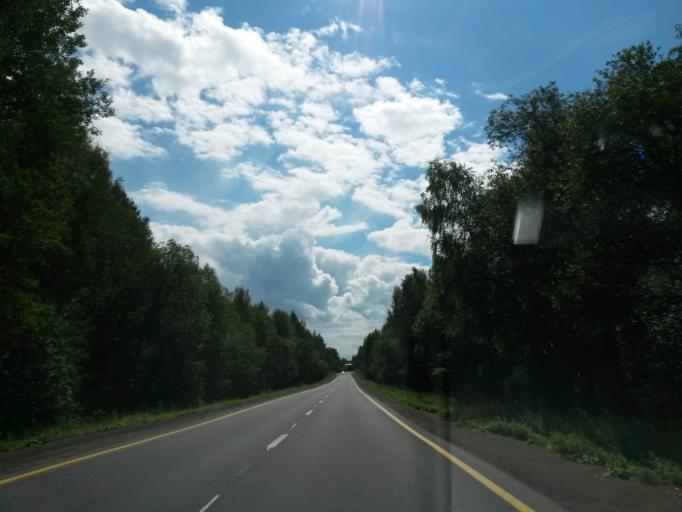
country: RU
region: Jaroslavl
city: Gavrilov-Yam
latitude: 57.2872
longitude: 39.9529
